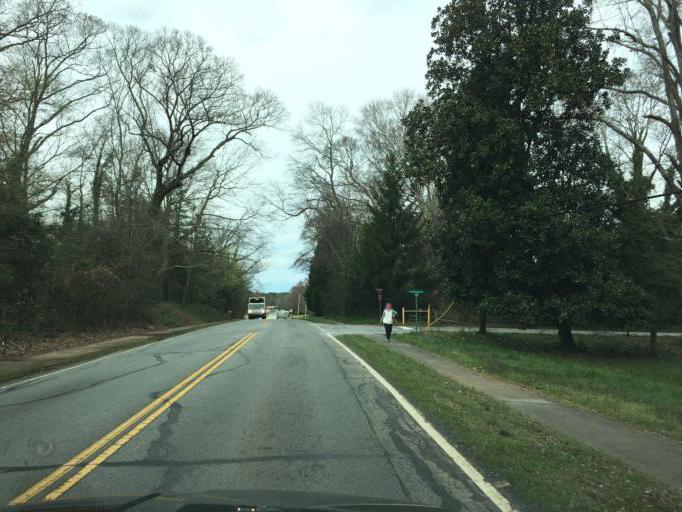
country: US
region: South Carolina
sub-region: Anderson County
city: Pendleton
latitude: 34.6705
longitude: -82.8059
